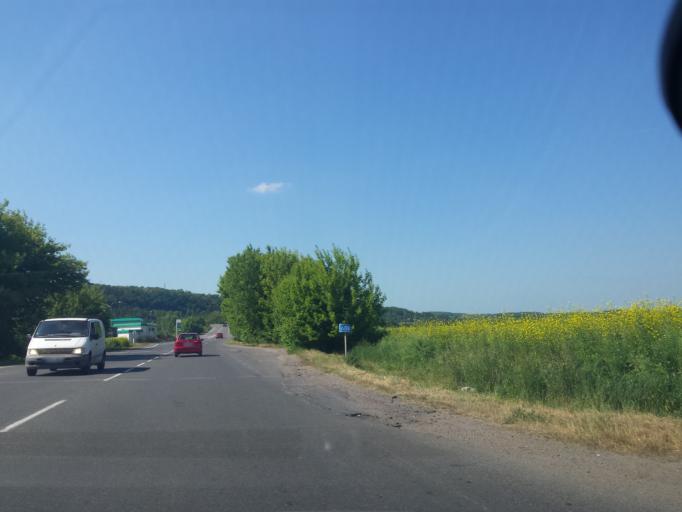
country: CZ
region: Central Bohemia
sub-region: Okres Melnik
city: Veltrusy
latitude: 50.2853
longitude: 14.3133
